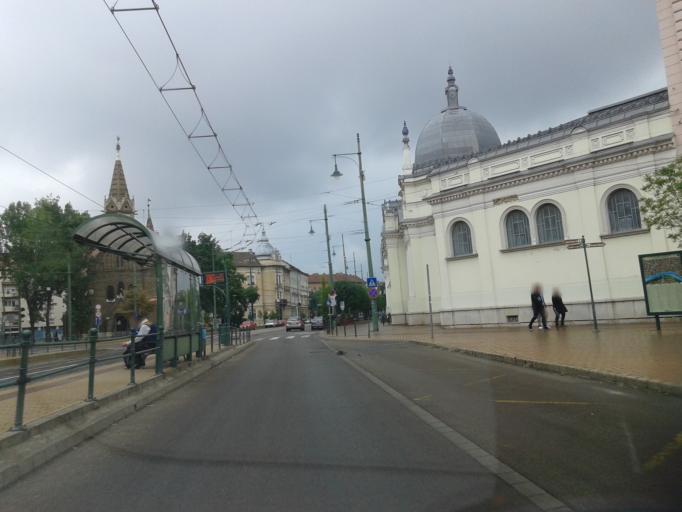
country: HU
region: Csongrad
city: Szeged
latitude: 46.2559
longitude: 20.1486
